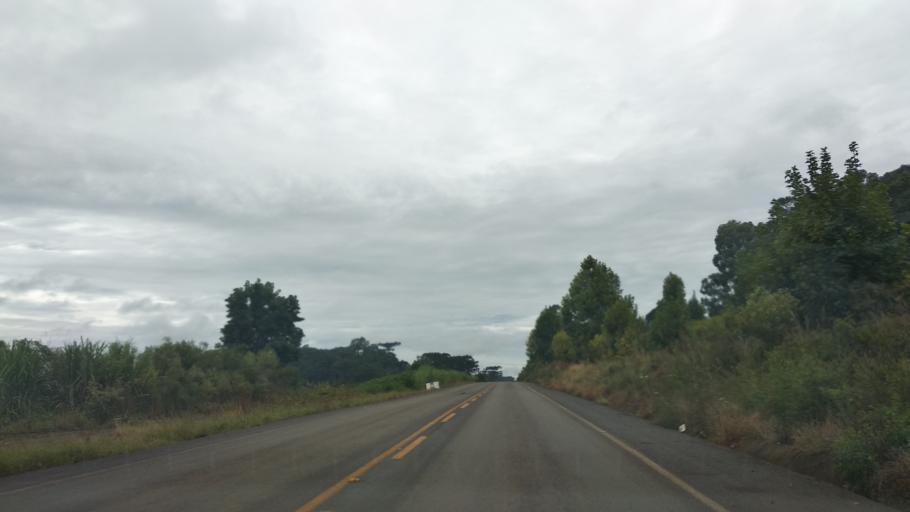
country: BR
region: Santa Catarina
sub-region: Videira
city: Videira
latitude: -27.0243
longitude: -51.1614
